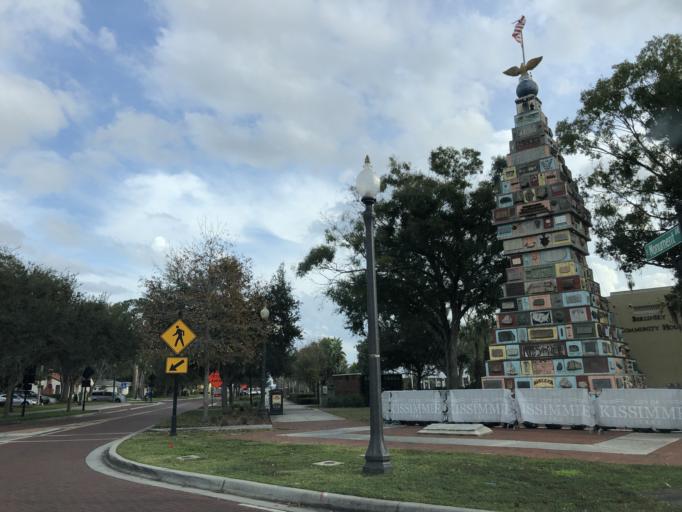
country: US
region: Florida
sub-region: Osceola County
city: Kissimmee
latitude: 28.2920
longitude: -81.4047
